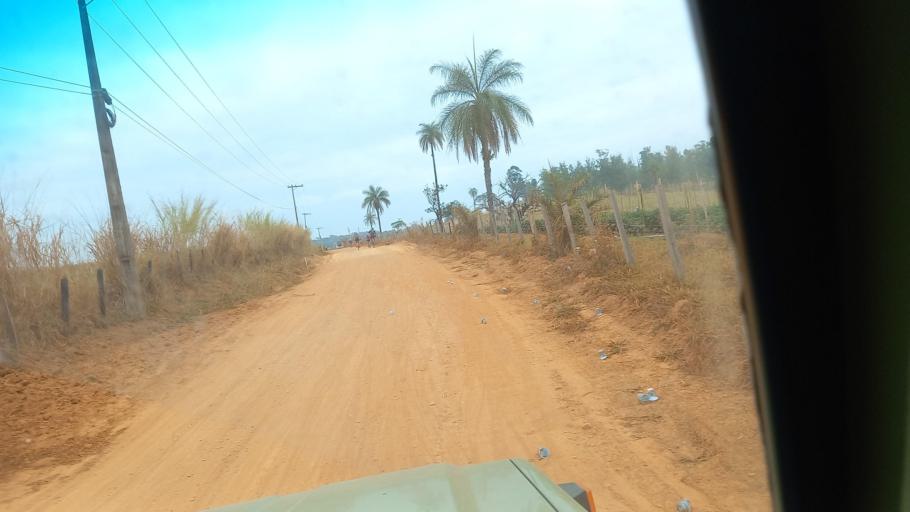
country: BR
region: Sao Paulo
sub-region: Moji-Guacu
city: Mogi-Gaucu
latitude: -22.3118
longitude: -46.8379
